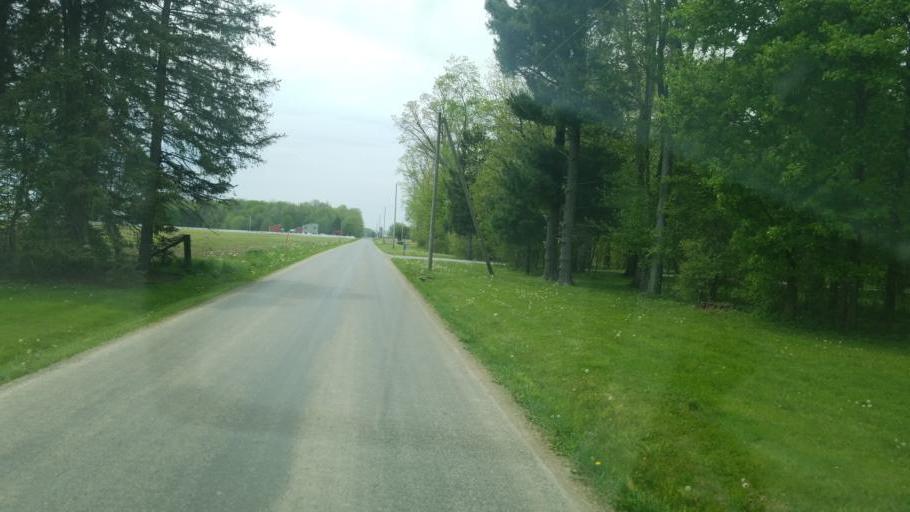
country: US
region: Ohio
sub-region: Richland County
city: Shelby
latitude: 40.9303
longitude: -82.6886
